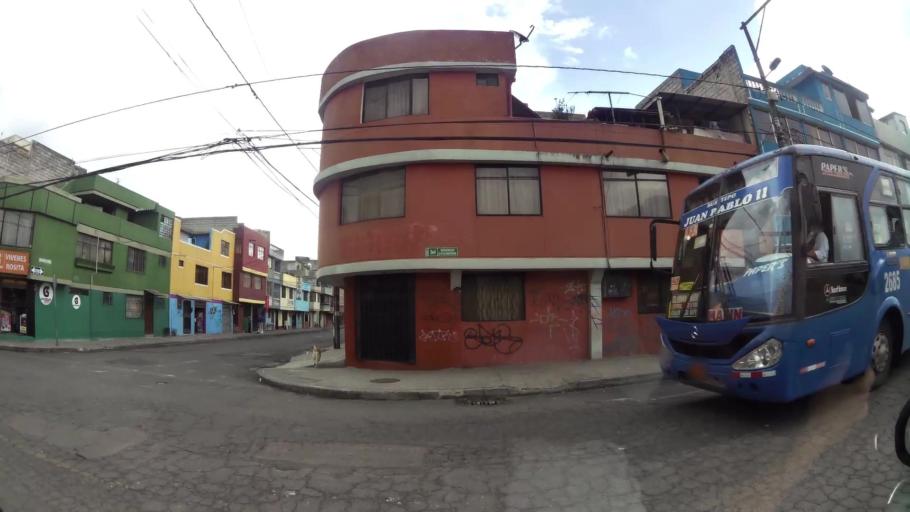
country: EC
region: Pichincha
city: Quito
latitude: -0.2672
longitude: -78.5368
